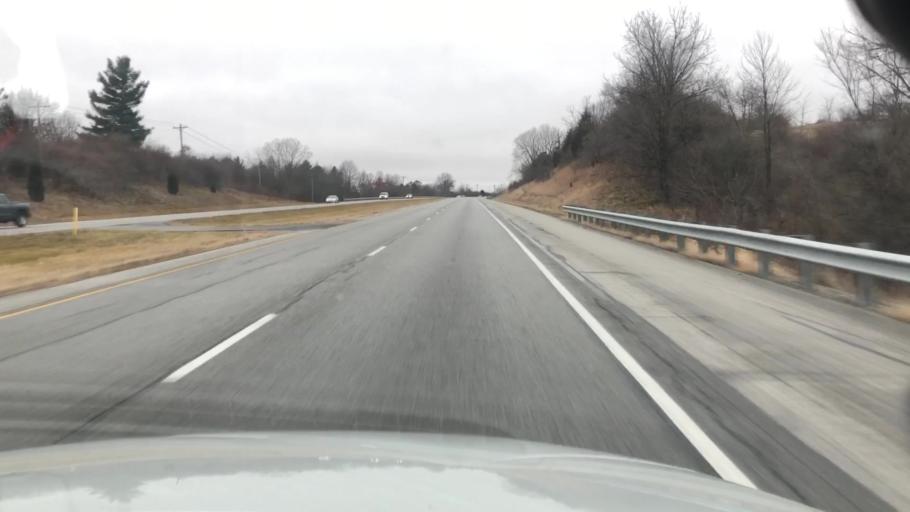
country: US
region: Indiana
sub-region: Whitley County
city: South Whitley
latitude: 41.1782
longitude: -85.6082
